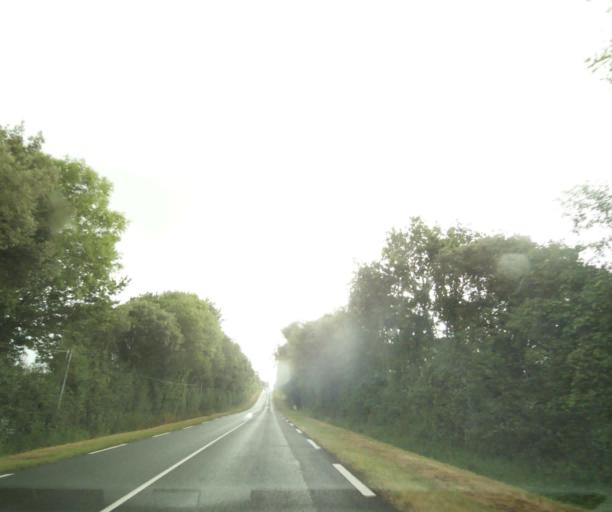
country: FR
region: Pays de la Loire
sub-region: Departement de la Vendee
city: Saint-Hilaire-de-Talmont
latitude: 46.4728
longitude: -1.5432
